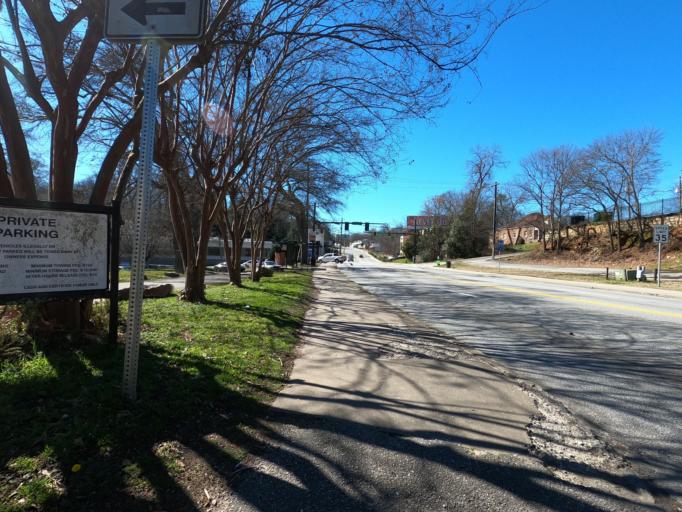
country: US
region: Georgia
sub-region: Clarke County
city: Athens
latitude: 33.9564
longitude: -83.3806
